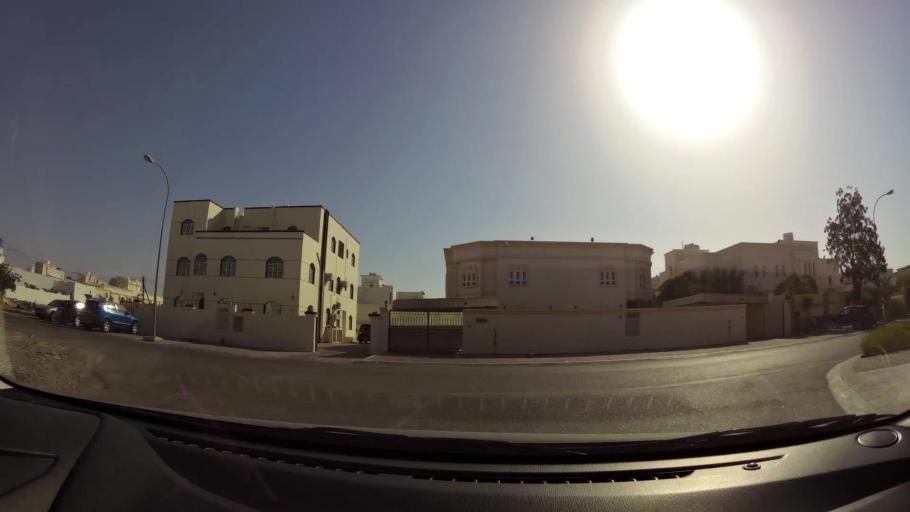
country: OM
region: Muhafazat Masqat
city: As Sib al Jadidah
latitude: 23.6193
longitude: 58.2081
